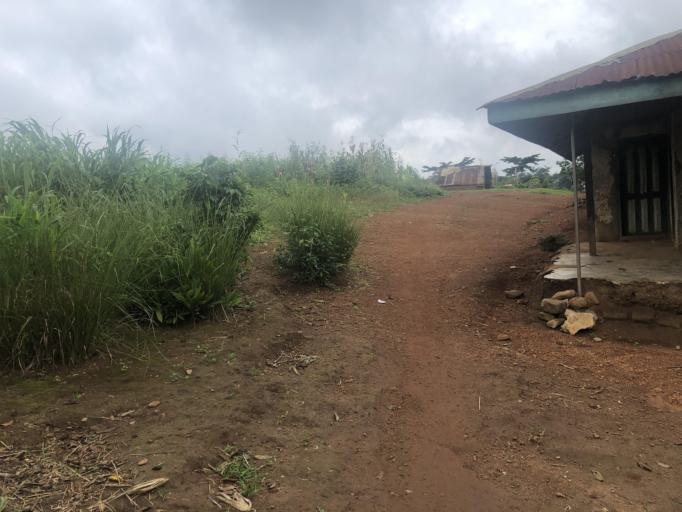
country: SL
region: Eastern Province
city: Kailahun
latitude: 8.2654
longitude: -10.5636
